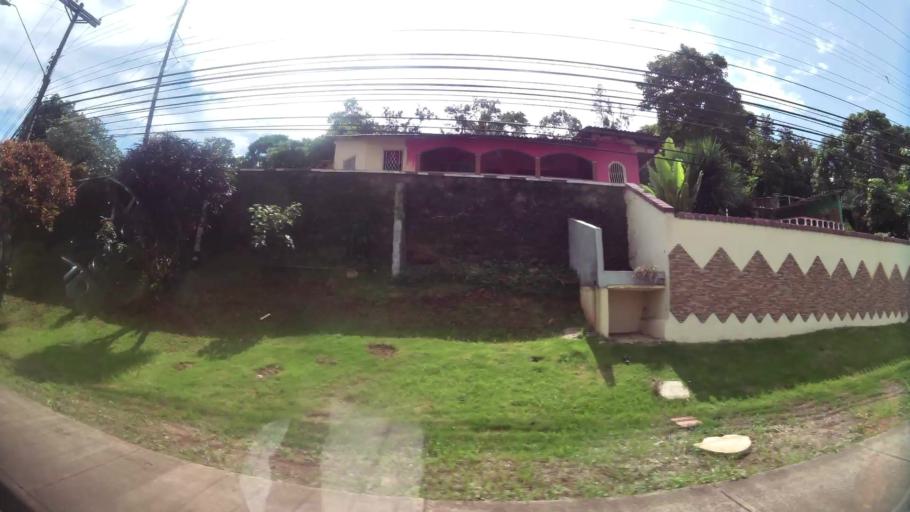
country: PA
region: Panama
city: Vista Alegre
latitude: 8.9330
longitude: -79.6972
